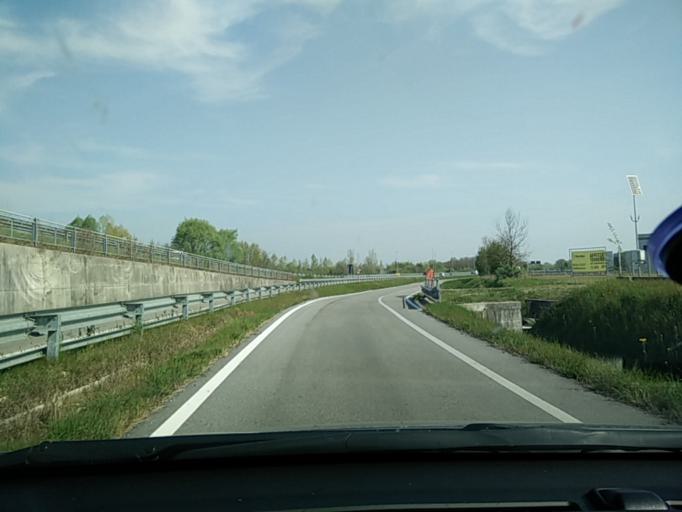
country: IT
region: Friuli Venezia Giulia
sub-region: Provincia di Pordenone
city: Fiume Veneto
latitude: 45.9491
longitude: 12.7200
